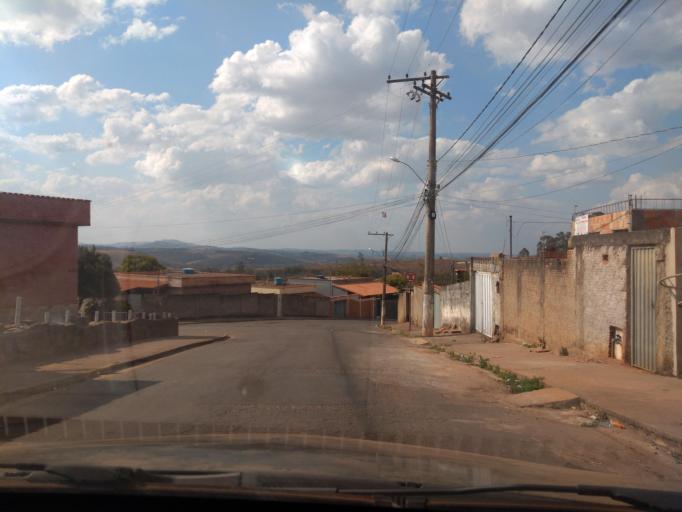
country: BR
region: Minas Gerais
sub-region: Tres Coracoes
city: Tres Coracoes
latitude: -21.6854
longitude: -45.2347
